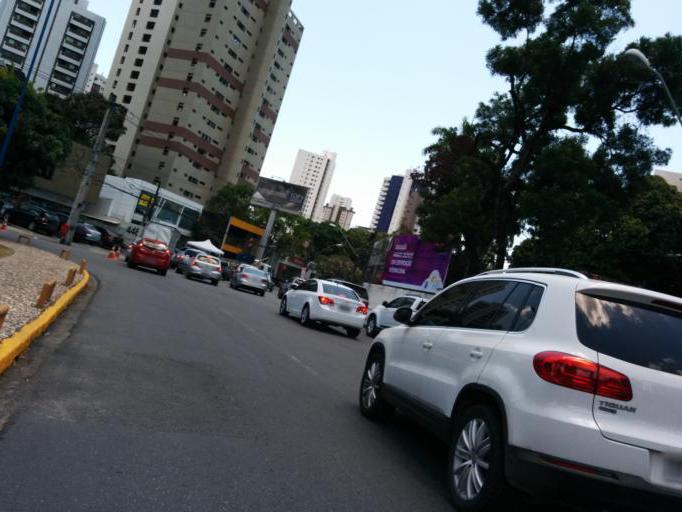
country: BR
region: Pernambuco
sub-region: Recife
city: Recife
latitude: -8.0334
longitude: -34.9104
